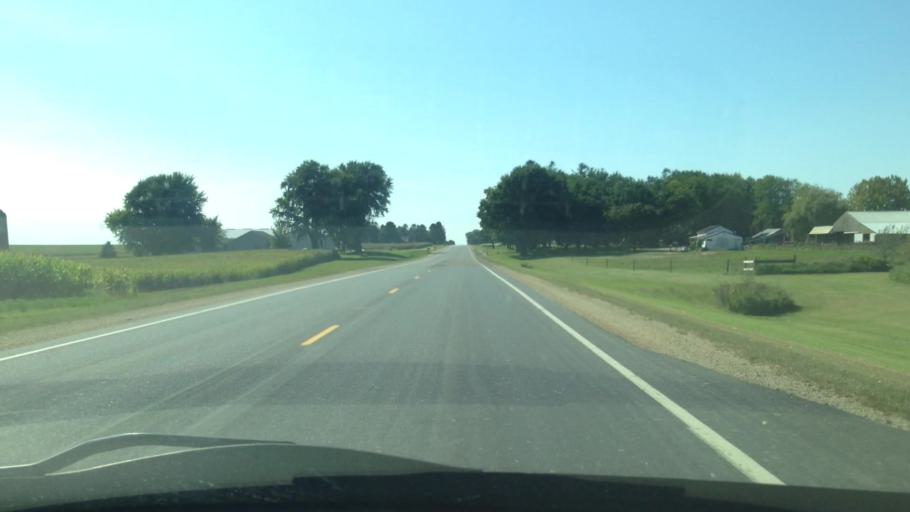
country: US
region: Minnesota
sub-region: Winona County
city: Lewiston
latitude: 43.9696
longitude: -91.8191
